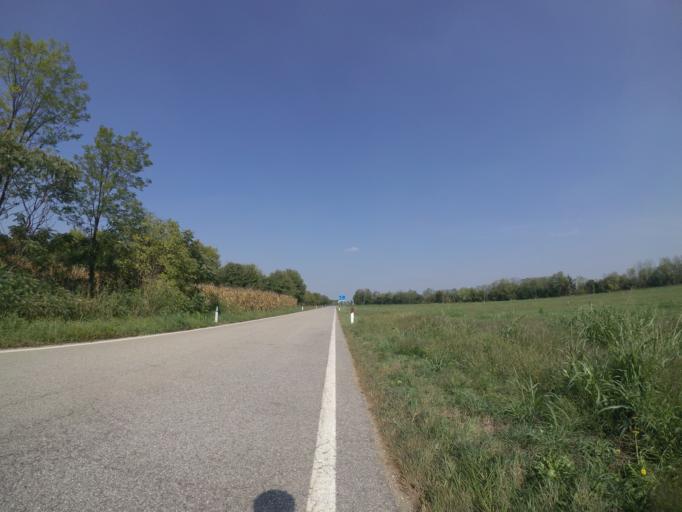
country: IT
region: Friuli Venezia Giulia
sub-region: Provincia di Udine
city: Codroipo
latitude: 45.9809
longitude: 12.9911
